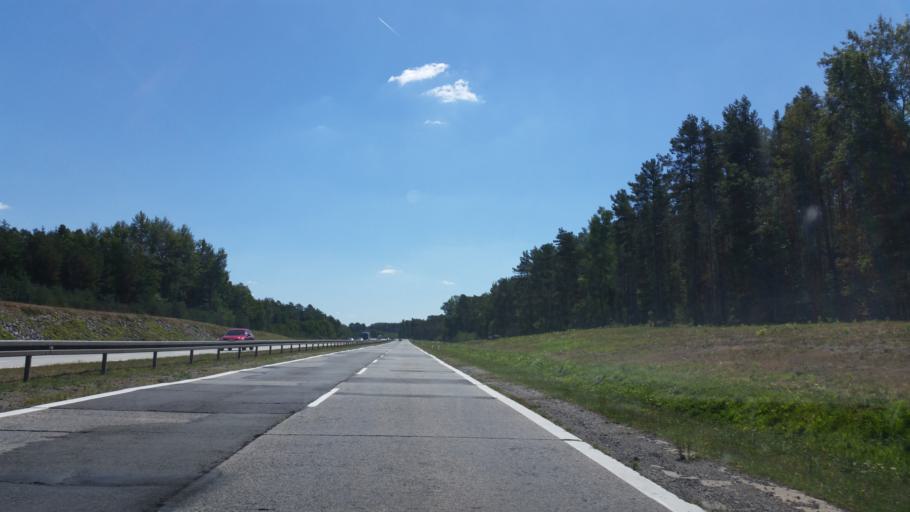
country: PL
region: Lubusz
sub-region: Powiat zarski
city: Sieniawa Zarska
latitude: 51.5739
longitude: 15.0329
